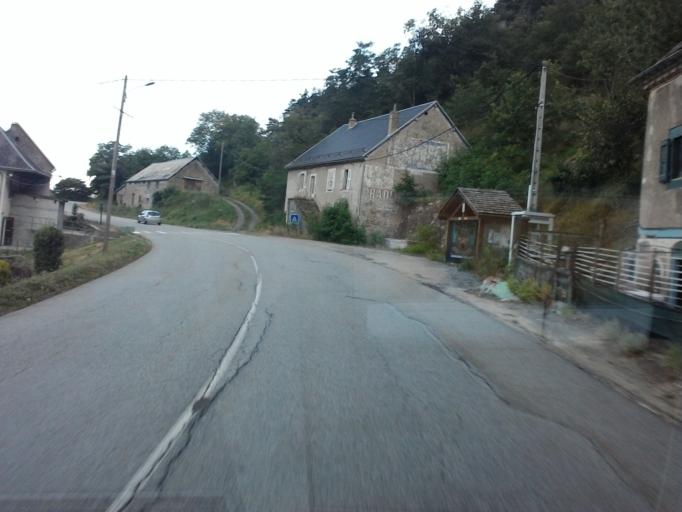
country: FR
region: Rhone-Alpes
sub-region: Departement de l'Isere
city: La Mure
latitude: 44.8406
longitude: 5.8759
